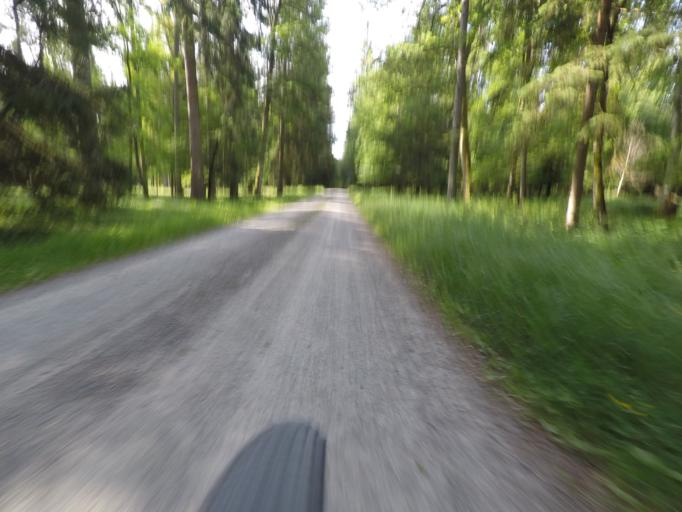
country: DE
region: Baden-Wuerttemberg
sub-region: Regierungsbezirk Stuttgart
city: Weil im Schonbuch
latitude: 48.5803
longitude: 9.0590
